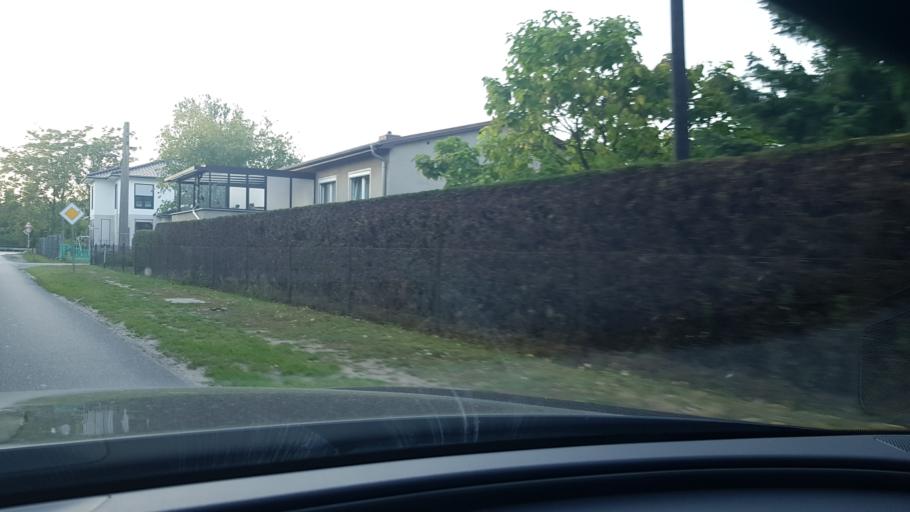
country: DE
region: Brandenburg
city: Brieselang
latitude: 52.5888
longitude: 12.9788
